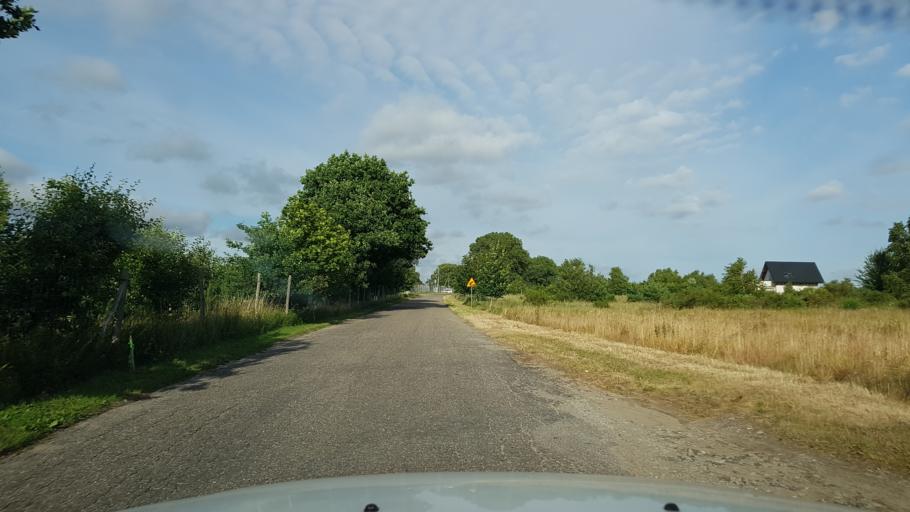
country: PL
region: West Pomeranian Voivodeship
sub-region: Powiat kolobrzeski
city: Grzybowo
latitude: 54.0913
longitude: 15.5389
